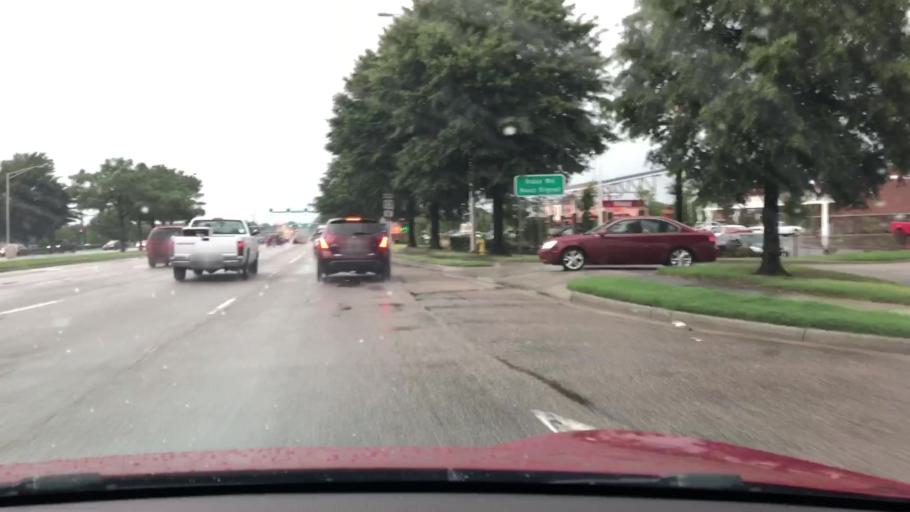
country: US
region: Virginia
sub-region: City of Norfolk
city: Norfolk
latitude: 36.8602
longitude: -76.2099
